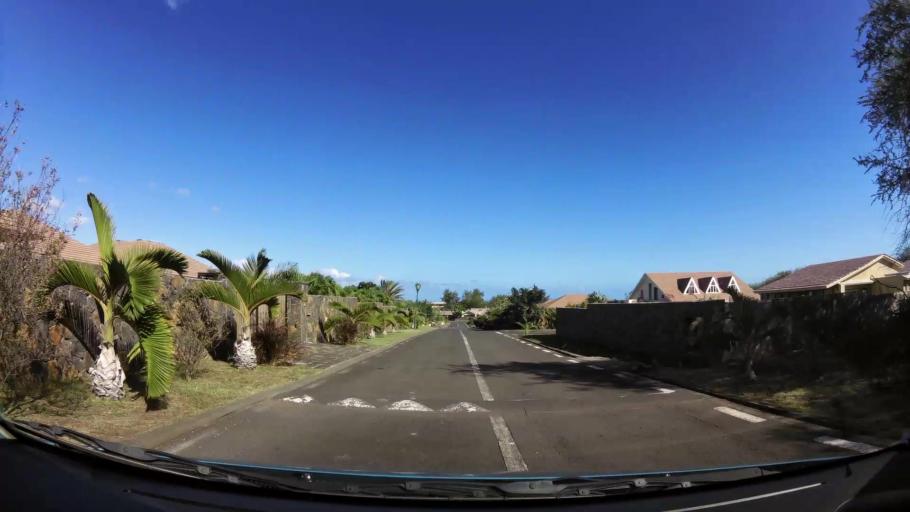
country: MU
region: Black River
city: Tamarin
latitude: -20.3409
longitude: 57.3672
